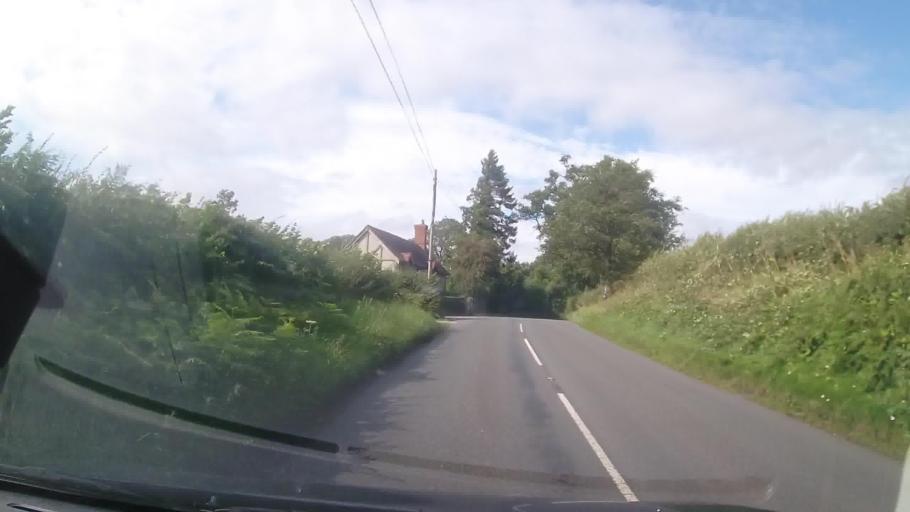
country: GB
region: England
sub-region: Shropshire
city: Acton
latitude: 52.4419
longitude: -3.0348
